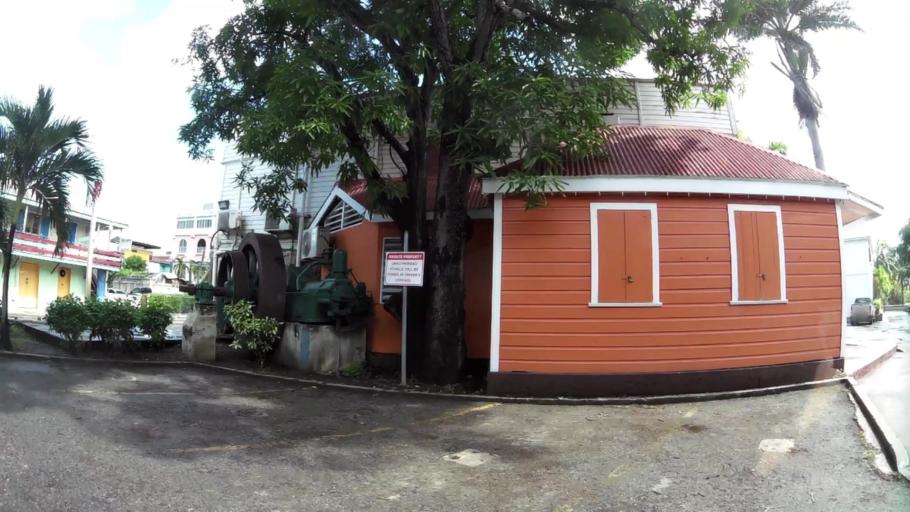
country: AG
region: Saint John
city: Saint John's
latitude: 17.1204
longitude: -61.8461
